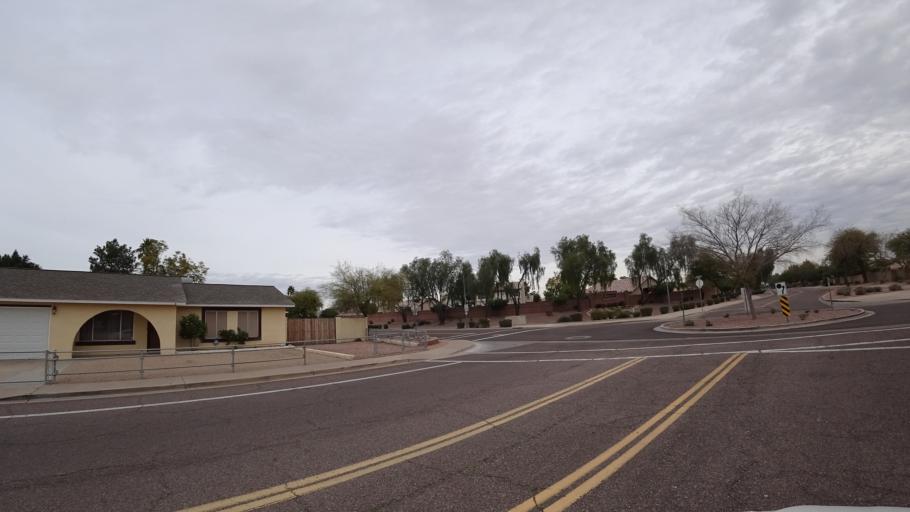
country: US
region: Arizona
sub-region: Maricopa County
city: Peoria
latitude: 33.6472
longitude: -112.1780
